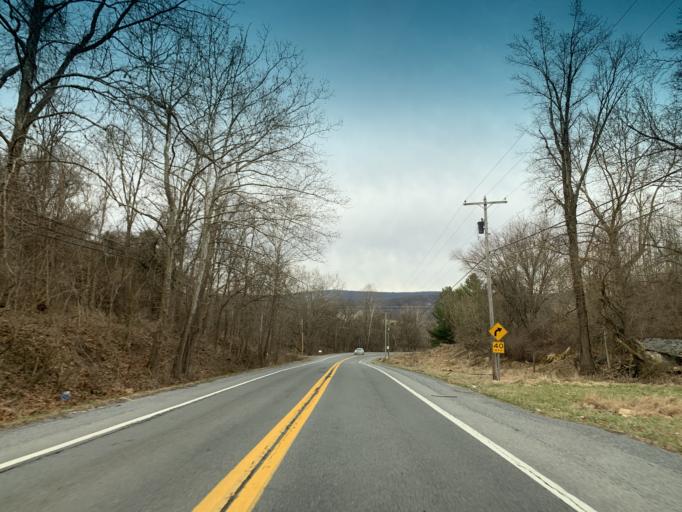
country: US
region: West Virginia
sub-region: Jefferson County
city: Shannondale
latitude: 39.2592
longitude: -77.8250
